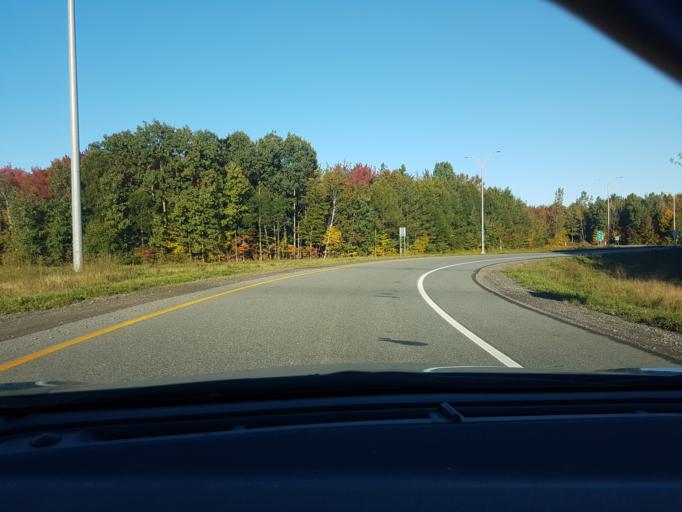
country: CA
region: Quebec
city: L'Ancienne-Lorette
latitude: 46.7862
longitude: -71.3267
